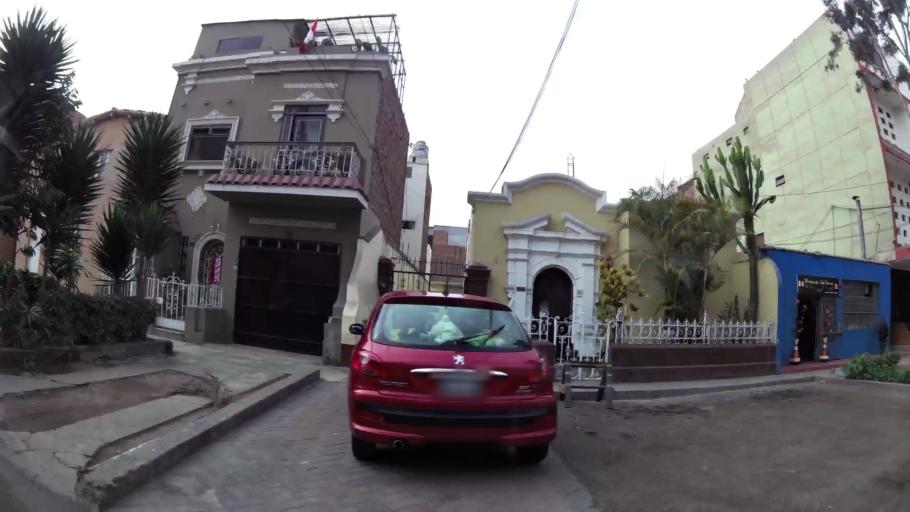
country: PE
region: Lima
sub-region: Lima
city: San Isidro
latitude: -12.0817
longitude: -77.0516
